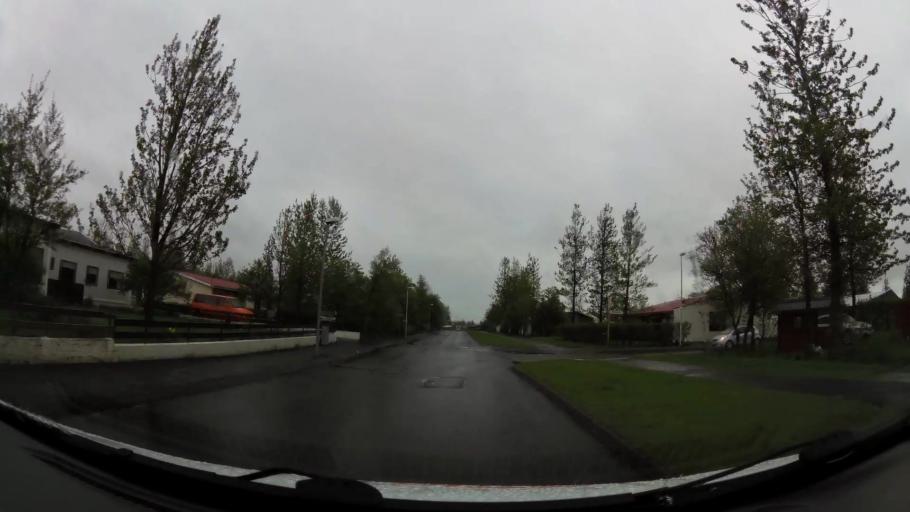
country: IS
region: South
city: Hveragerdi
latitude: 64.0010
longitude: -21.1967
